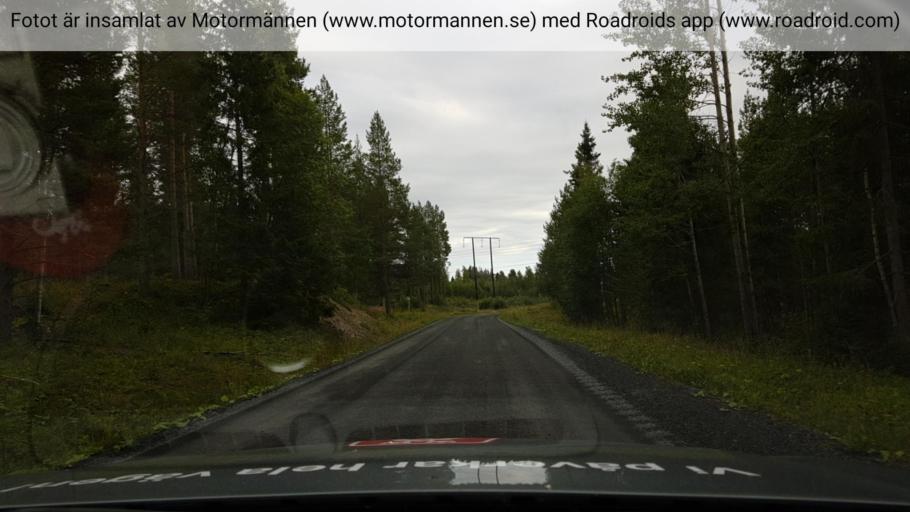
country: SE
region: Jaemtland
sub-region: Krokoms Kommun
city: Valla
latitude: 63.3415
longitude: 14.0097
